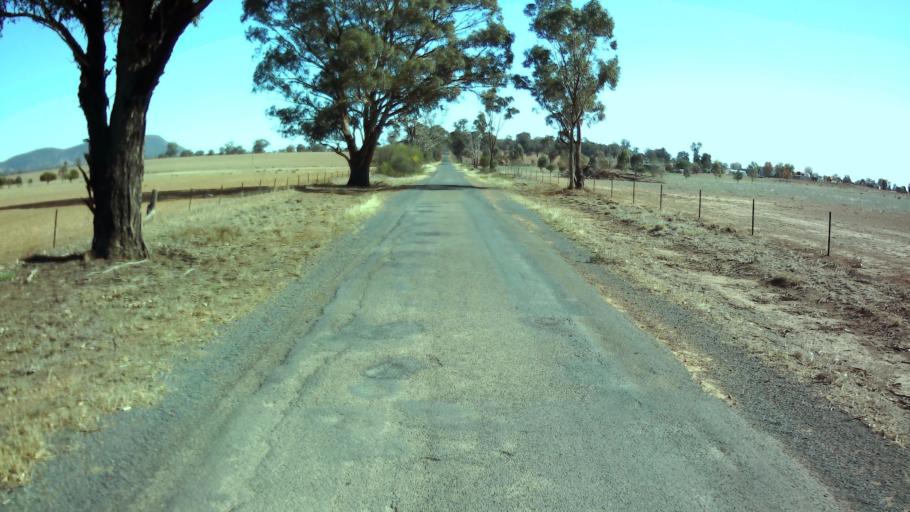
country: AU
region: New South Wales
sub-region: Weddin
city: Grenfell
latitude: -33.7952
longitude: 147.9567
